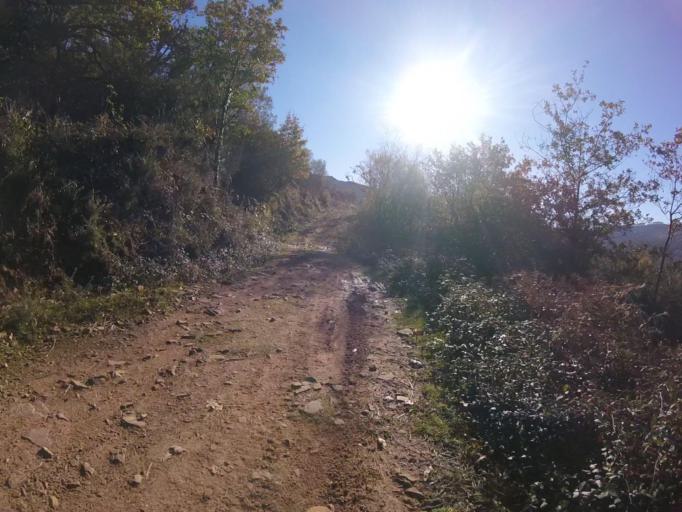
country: FR
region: Aquitaine
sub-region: Departement des Pyrenees-Atlantiques
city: Urrugne
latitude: 43.3186
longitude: -1.7283
